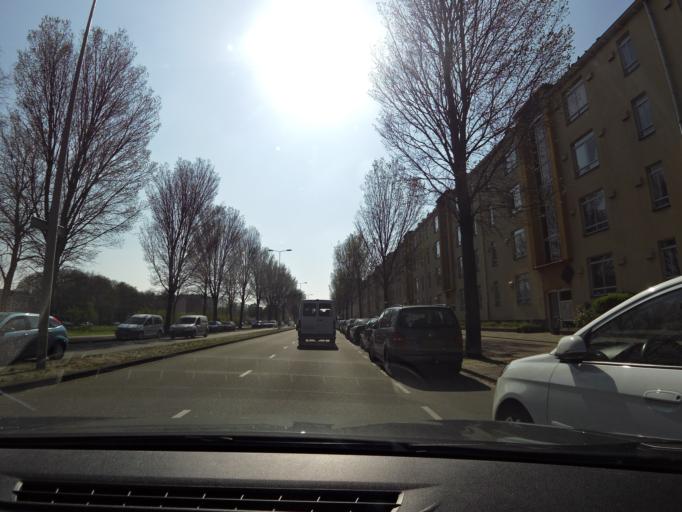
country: NL
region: South Holland
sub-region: Gemeente Den Haag
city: The Hague
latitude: 52.0533
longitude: 4.3044
